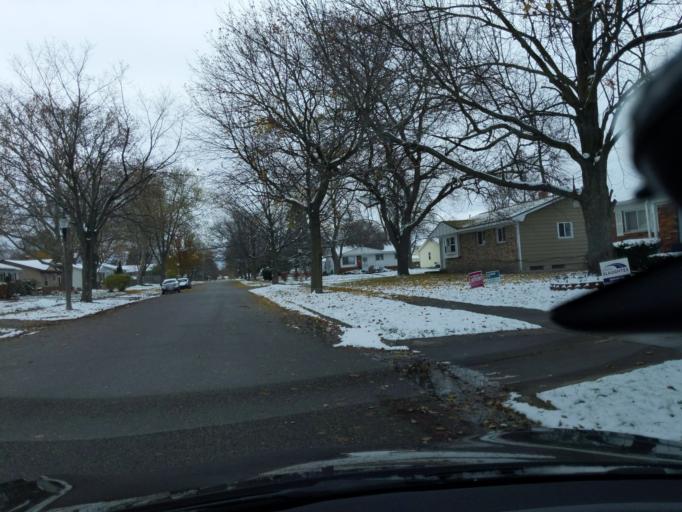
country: US
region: Michigan
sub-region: Eaton County
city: Waverly
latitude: 42.6848
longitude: -84.6006
